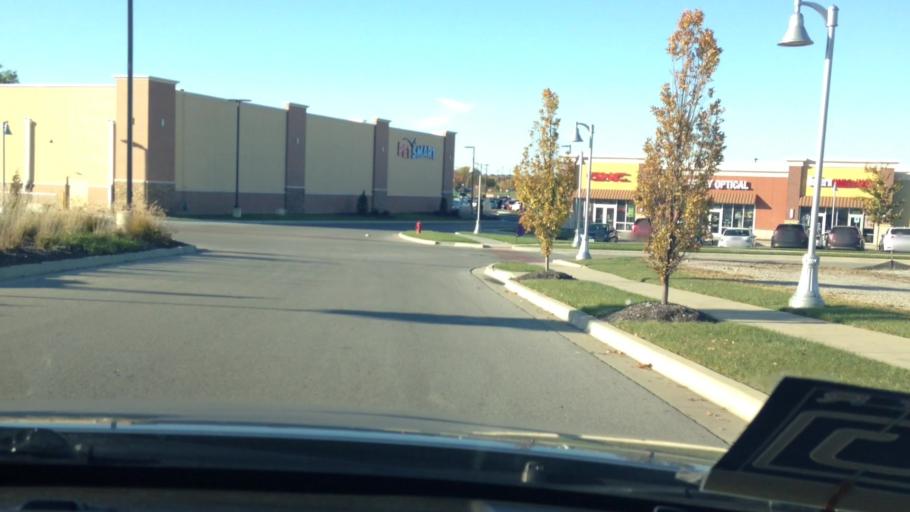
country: US
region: Missouri
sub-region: Clay County
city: Gladstone
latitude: 39.1880
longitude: -94.5466
